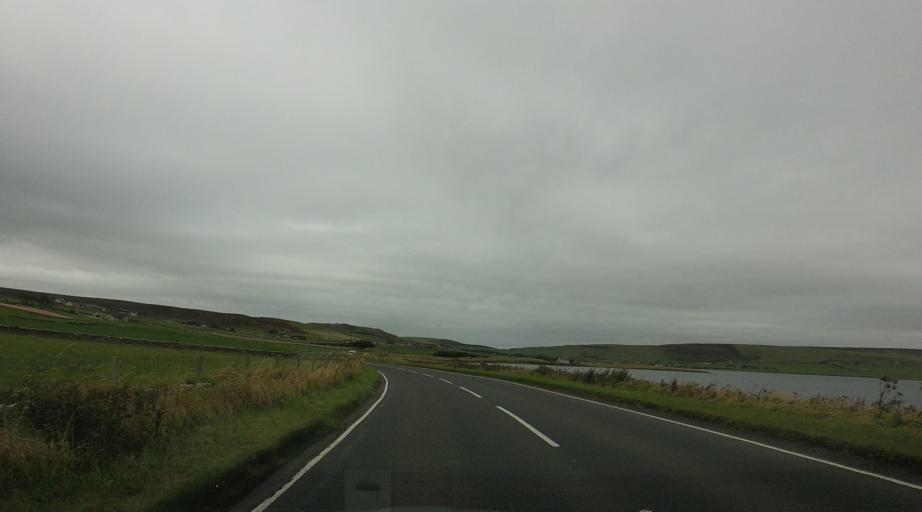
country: GB
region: Scotland
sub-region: Orkney Islands
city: Orkney
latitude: 58.9978
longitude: -3.0821
